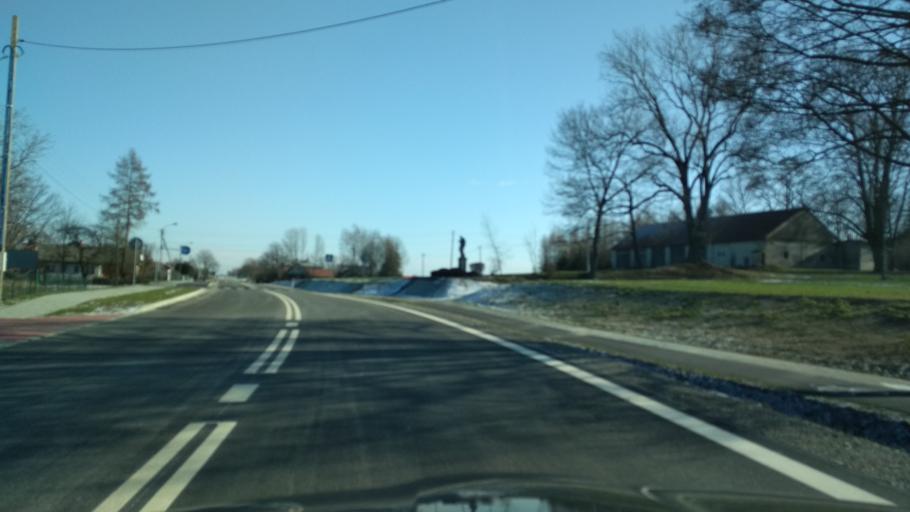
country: PL
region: Subcarpathian Voivodeship
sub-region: Powiat ropczycko-sedziszowski
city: Sedziszow Malopolski
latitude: 50.0698
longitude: 21.7343
